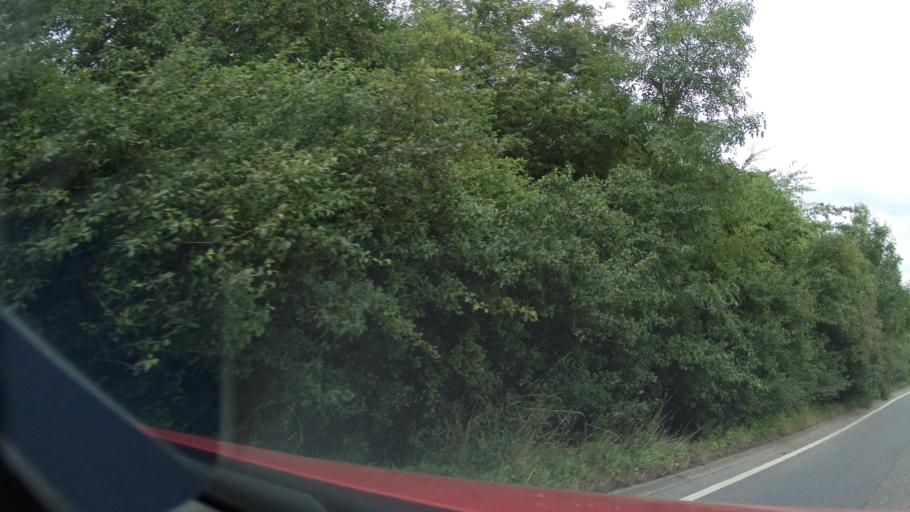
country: GB
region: England
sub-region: Northamptonshire
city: Geddington
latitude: 52.4444
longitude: -0.7355
